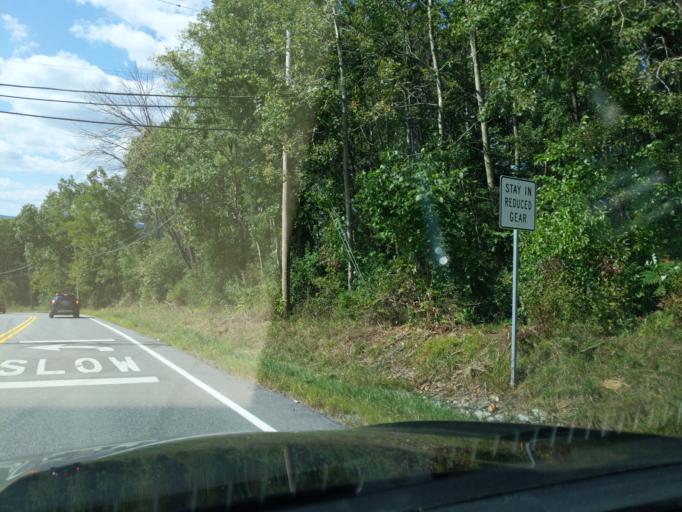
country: US
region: Pennsylvania
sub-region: Blair County
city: Greenwood
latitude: 40.5165
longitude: -78.3662
